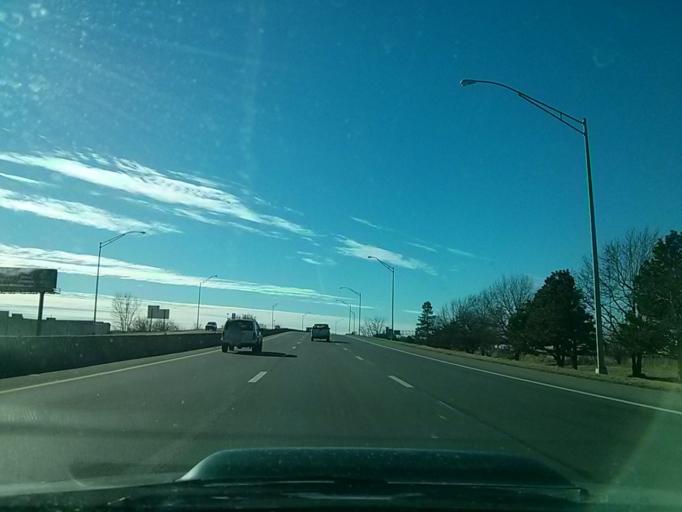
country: US
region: Oklahoma
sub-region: Tulsa County
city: Tulsa
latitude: 36.1214
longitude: -96.0091
